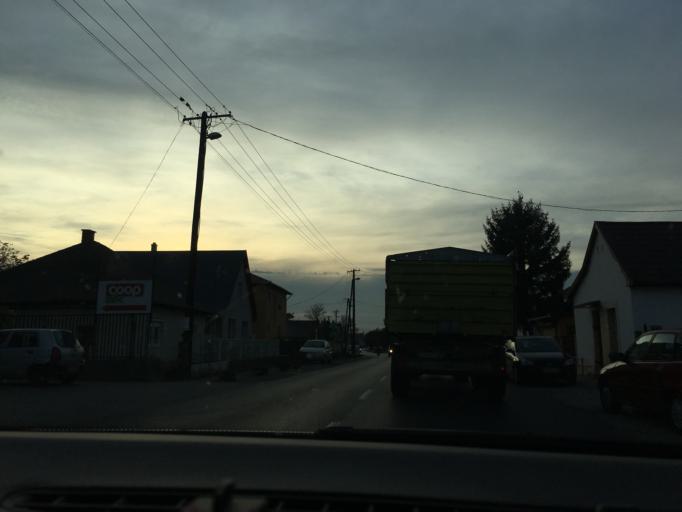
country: HU
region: Szabolcs-Szatmar-Bereg
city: Kallosemjen
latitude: 47.8589
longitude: 21.9303
